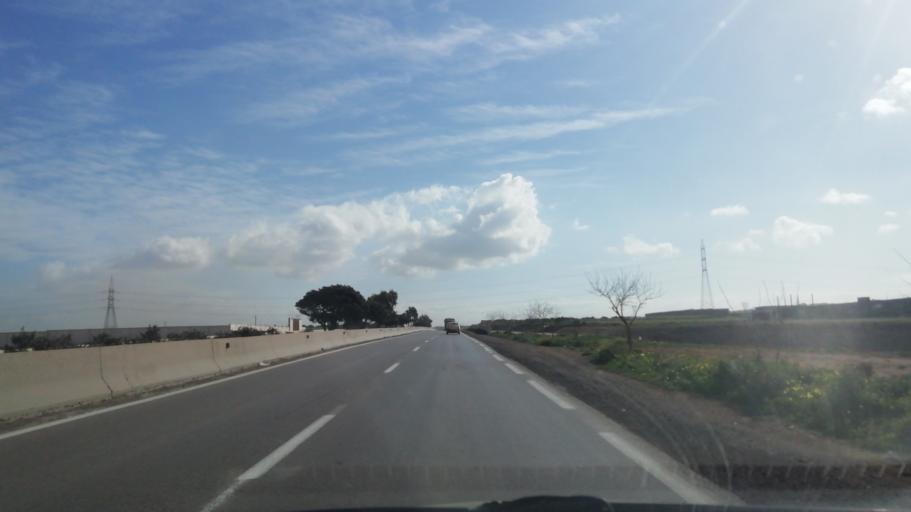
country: DZ
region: Oran
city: Ain el Bya
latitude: 35.7733
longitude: -0.2489
